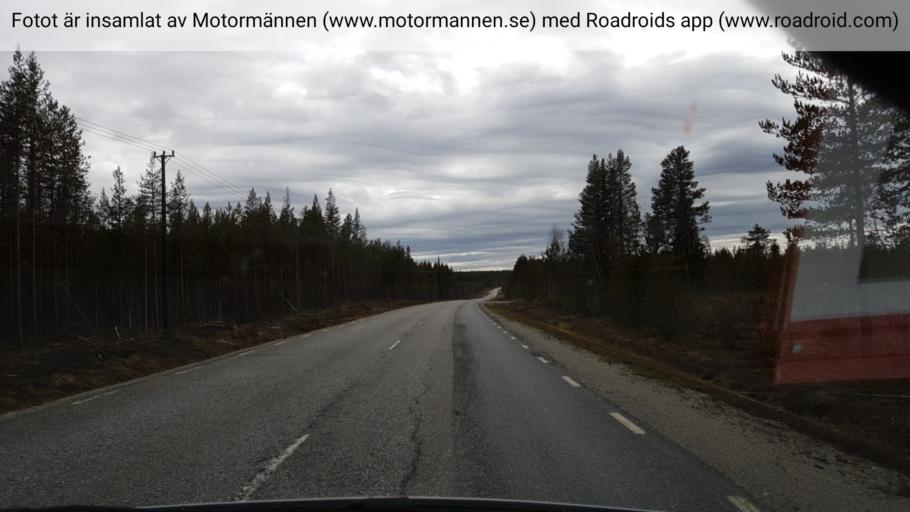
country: SE
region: Vaesterbotten
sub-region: Asele Kommun
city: Asele
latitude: 63.9281
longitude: 17.2629
